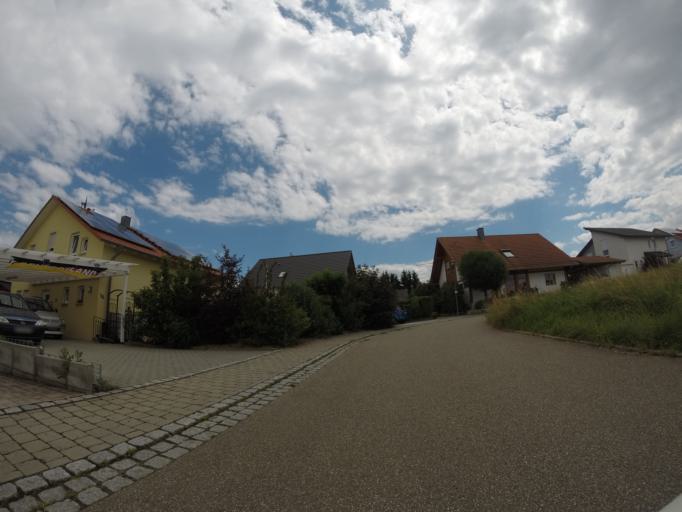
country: DE
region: Baden-Wuerttemberg
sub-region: Karlsruhe Region
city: Dobel
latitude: 48.8533
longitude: 8.5253
